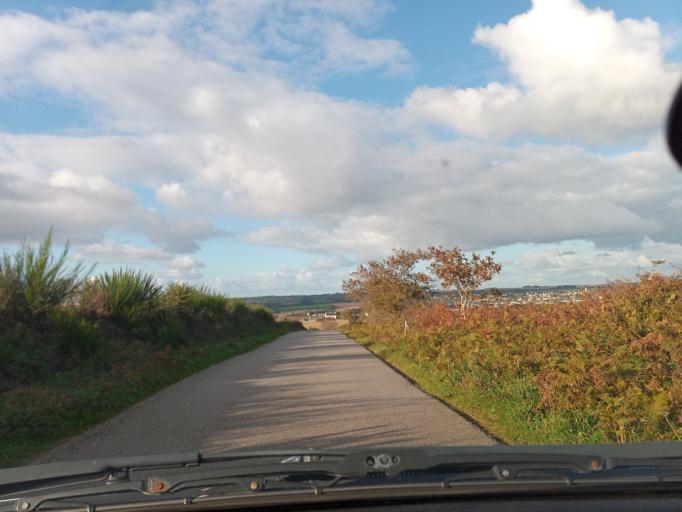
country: FR
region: Brittany
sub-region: Departement du Finistere
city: Plouhinec
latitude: 48.0258
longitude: -4.4981
